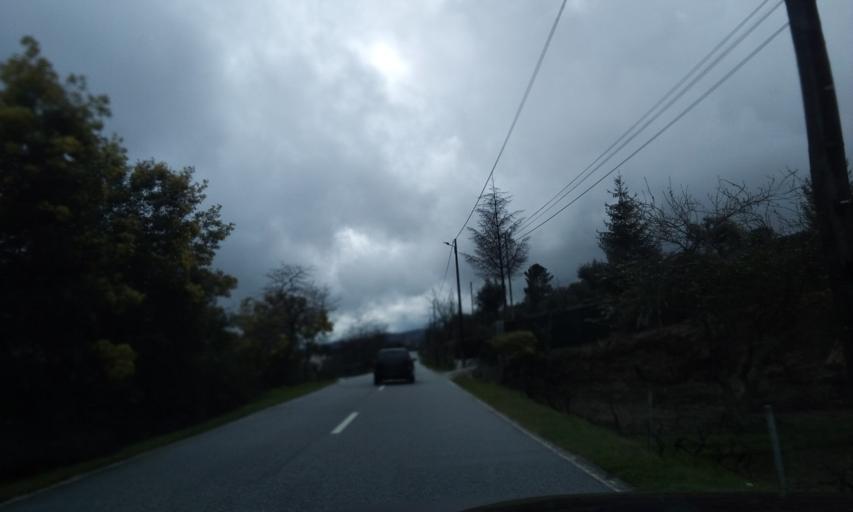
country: PT
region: Guarda
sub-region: Fornos de Algodres
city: Fornos de Algodres
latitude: 40.6115
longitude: -7.5626
